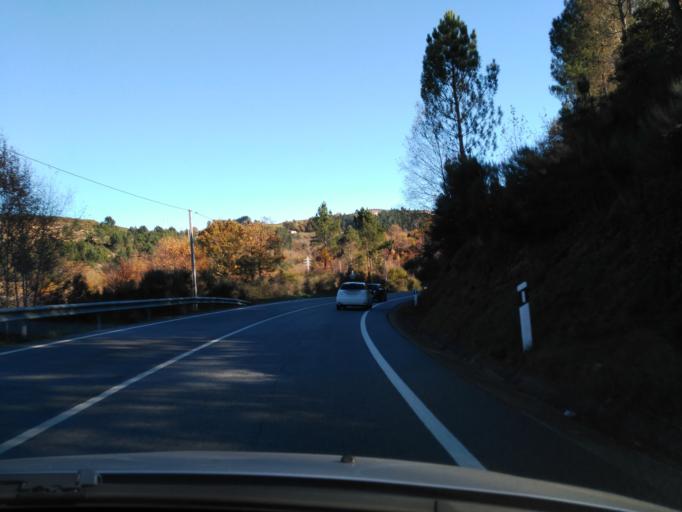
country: PT
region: Vila Real
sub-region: Montalegre
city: Montalegre
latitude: 41.7011
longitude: -7.9268
